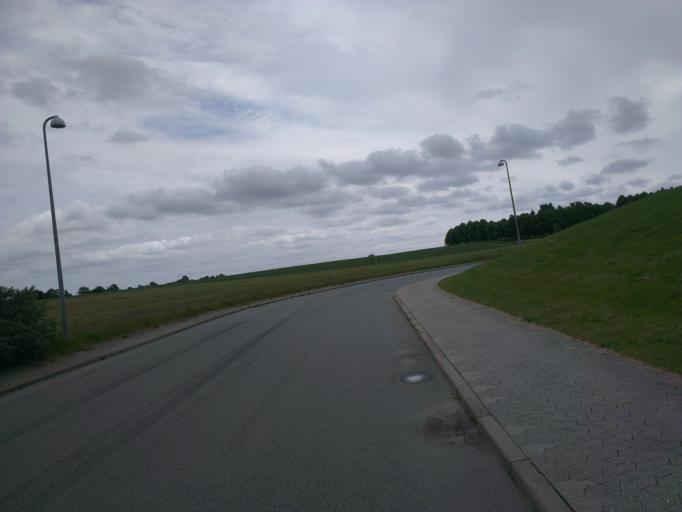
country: DK
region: Capital Region
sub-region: Frederikssund Kommune
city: Frederikssund
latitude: 55.8237
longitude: 12.1025
